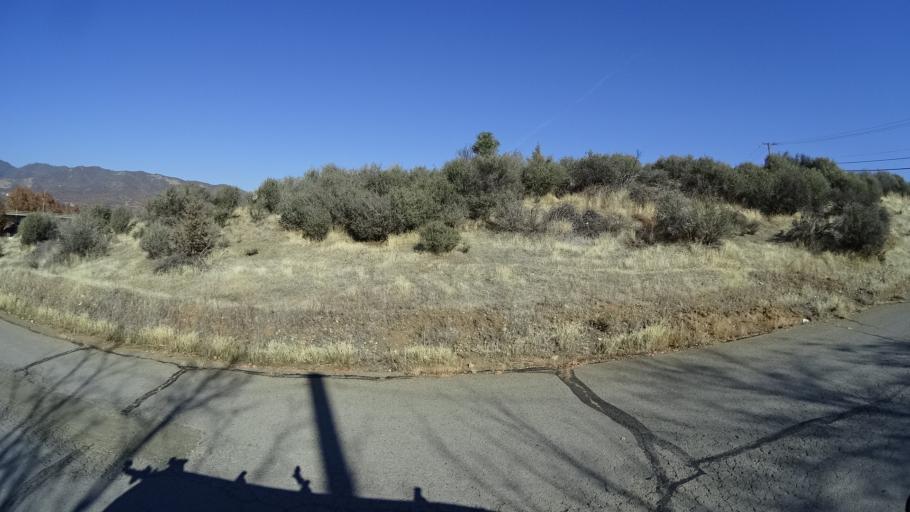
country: US
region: California
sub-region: Siskiyou County
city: Yreka
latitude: 41.7303
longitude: -122.6318
